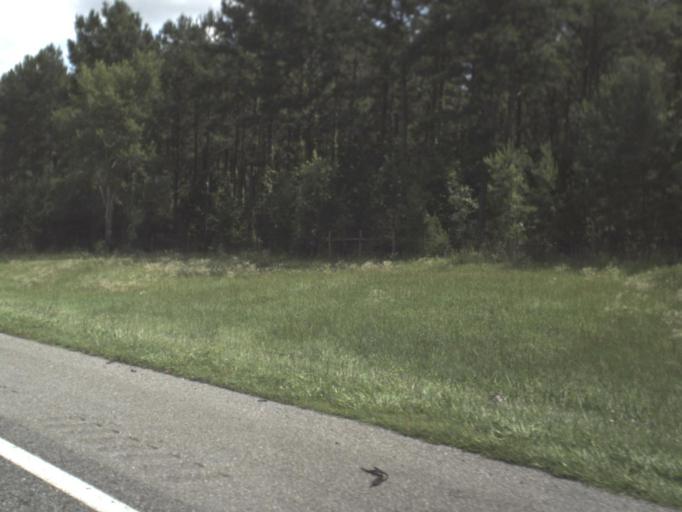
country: US
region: Florida
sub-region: Alachua County
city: High Springs
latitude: 29.8990
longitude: -82.5467
